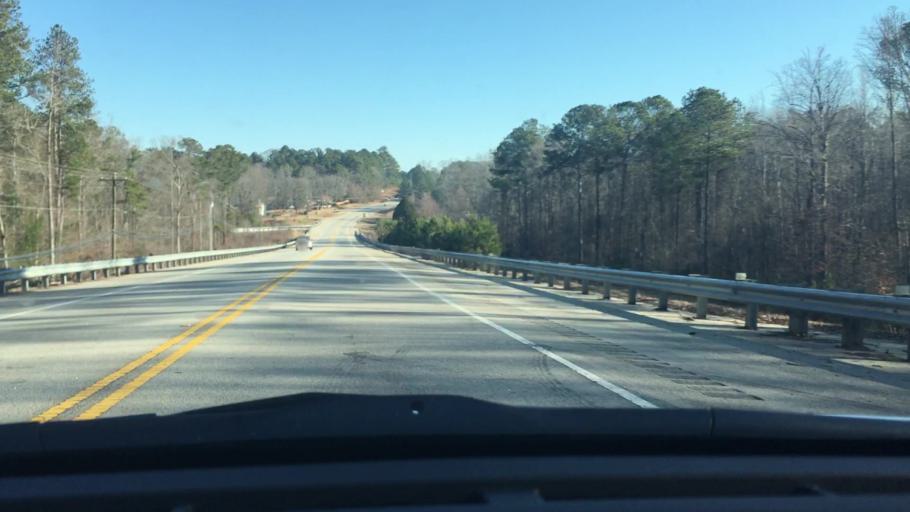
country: US
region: Georgia
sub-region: Henry County
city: McDonough
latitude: 33.4843
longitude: -84.0935
